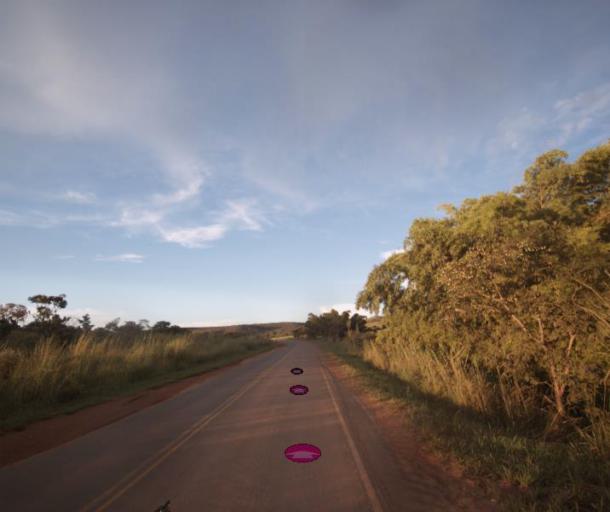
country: BR
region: Goias
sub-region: Anapolis
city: Anapolis
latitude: -16.1604
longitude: -48.8898
